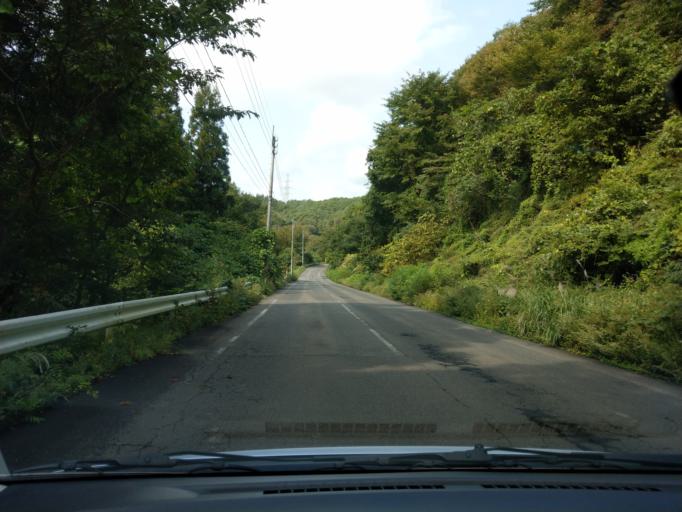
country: JP
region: Akita
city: Omagari
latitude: 39.4440
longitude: 140.3282
